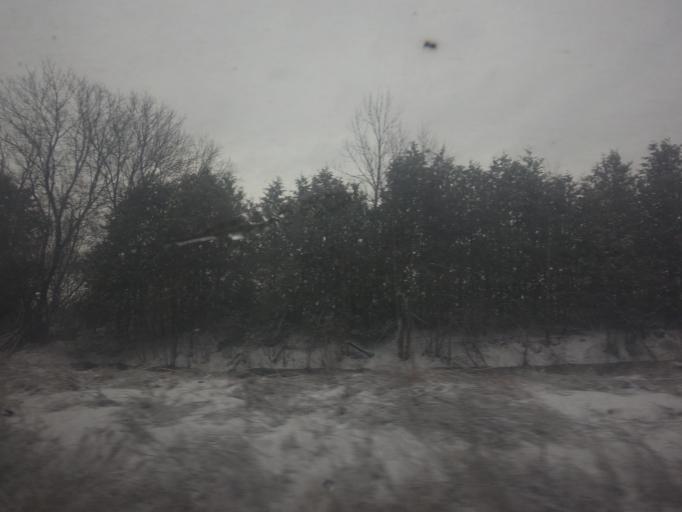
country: CA
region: Ontario
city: Bells Corners
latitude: 45.2003
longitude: -75.8151
